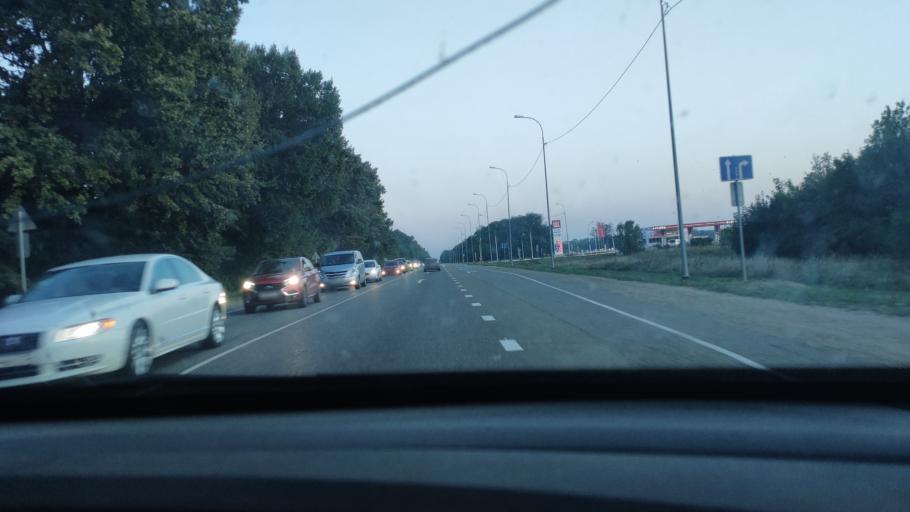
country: RU
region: Krasnodarskiy
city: Medvedovskaya
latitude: 45.4470
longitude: 38.9933
